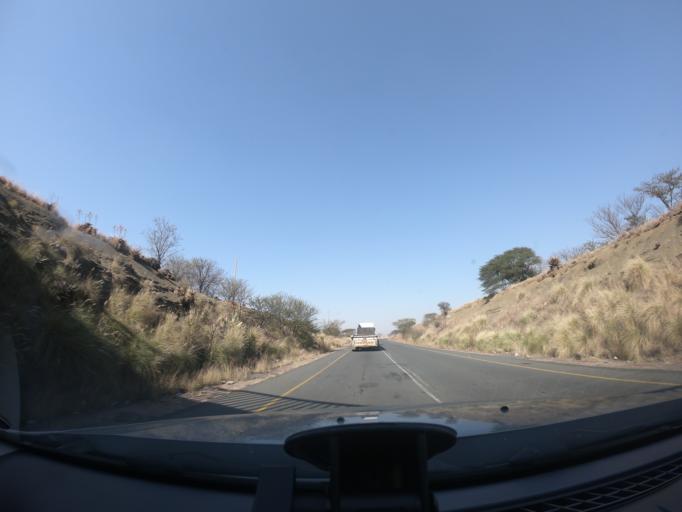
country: ZA
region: KwaZulu-Natal
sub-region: uThukela District Municipality
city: Ladysmith
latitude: -28.7506
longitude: 29.8222
